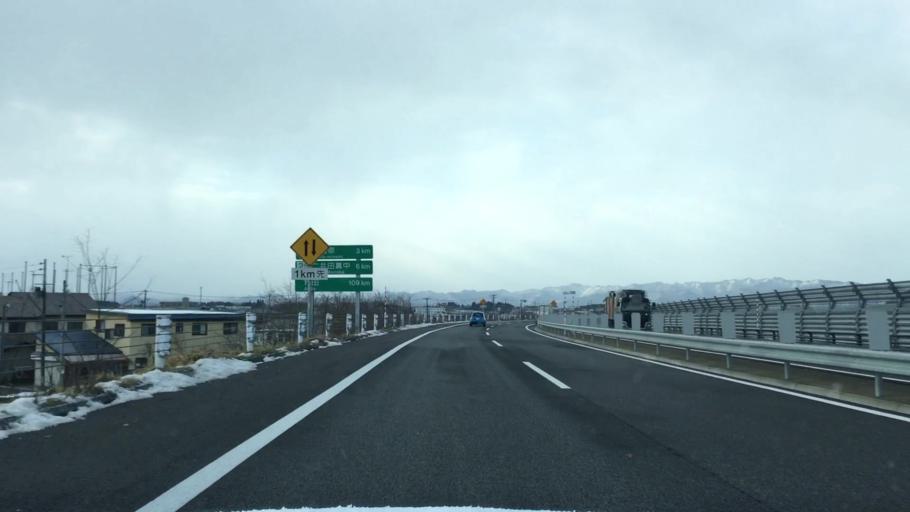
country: JP
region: Akita
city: Odate
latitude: 40.2942
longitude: 140.5529
